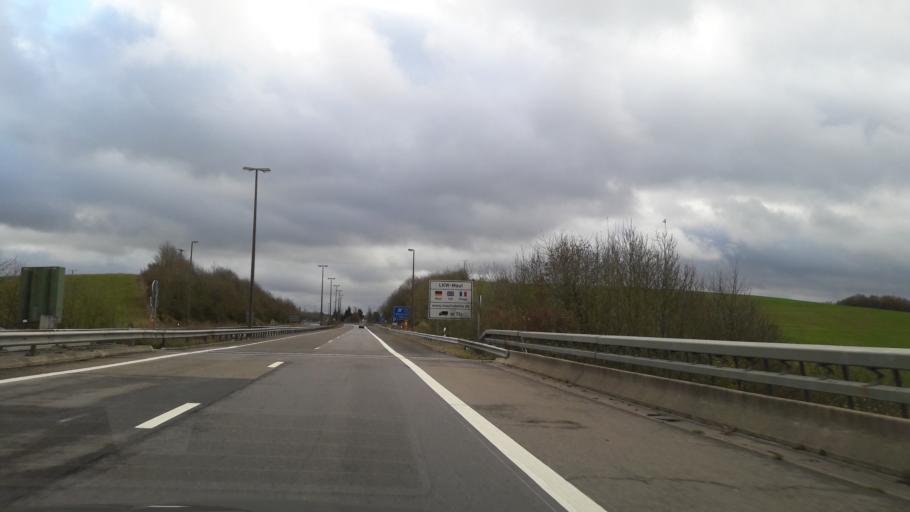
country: DE
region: Rheinland-Pfalz
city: Winterspelt
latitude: 50.2355
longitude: 6.1823
